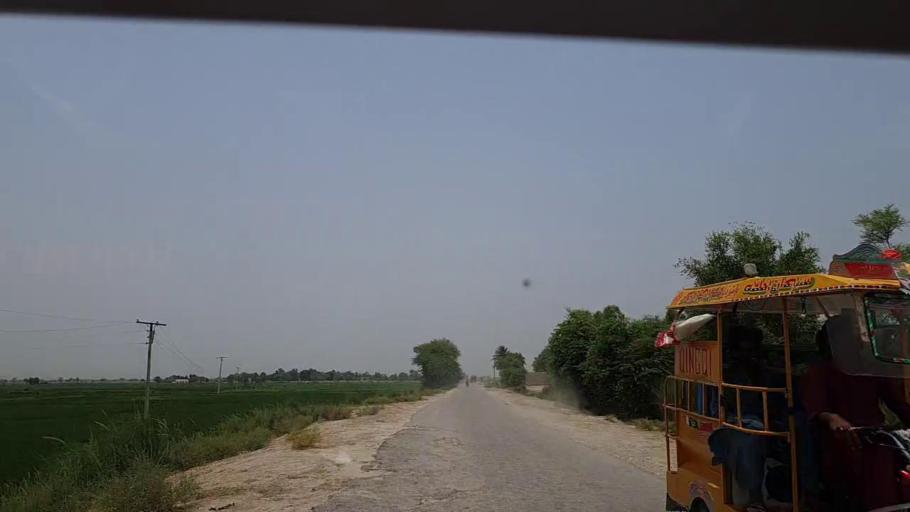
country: PK
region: Sindh
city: Khairpur Nathan Shah
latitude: 27.0099
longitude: 67.6700
